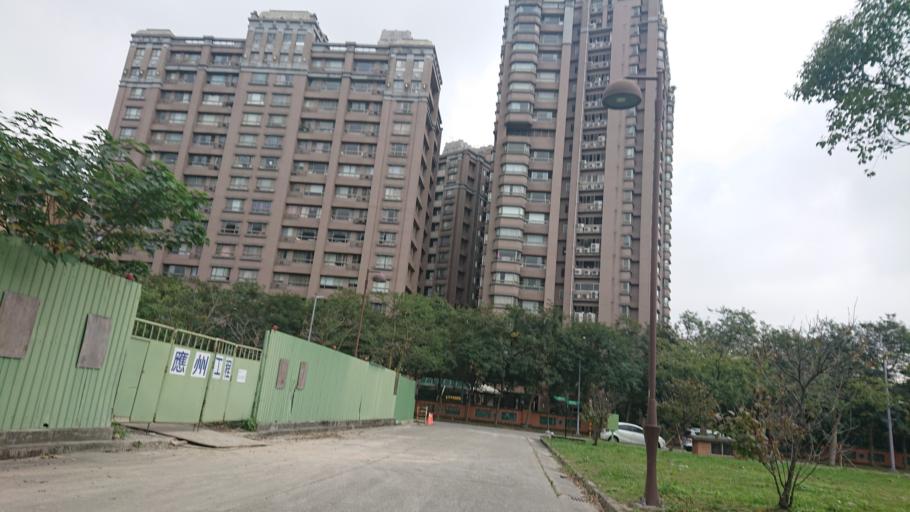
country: TW
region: Taiwan
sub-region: Taoyuan
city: Taoyuan
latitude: 24.9426
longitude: 121.3700
